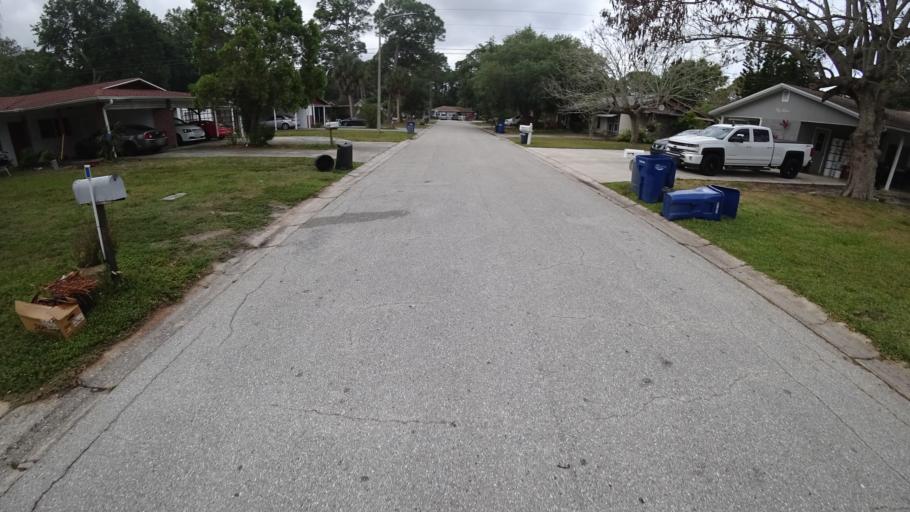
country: US
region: Florida
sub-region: Manatee County
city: South Bradenton
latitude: 27.4527
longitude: -82.5850
